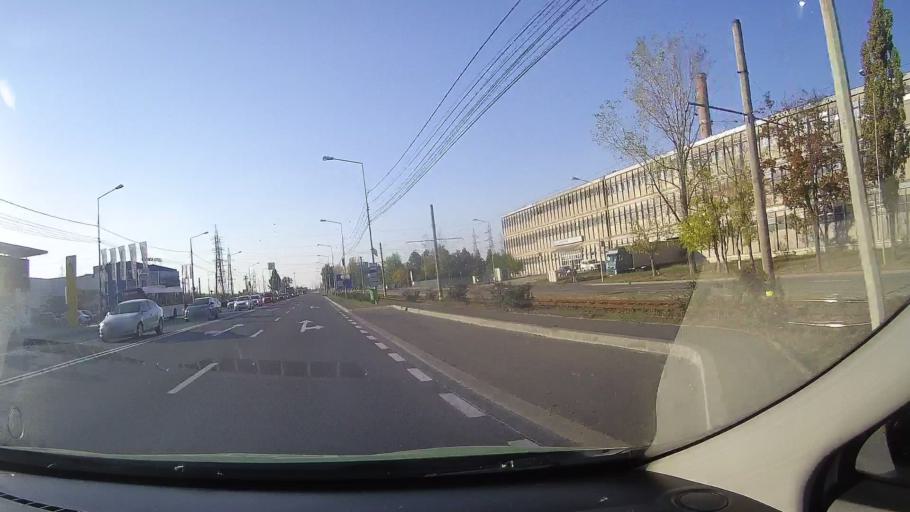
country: RO
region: Bihor
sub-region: Comuna Biharea
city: Oradea
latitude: 47.0803
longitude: 21.8940
